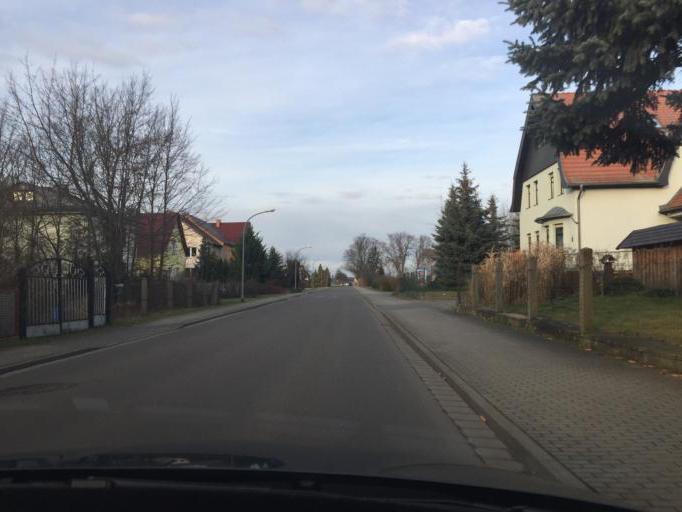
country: DE
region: Brandenburg
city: Forst
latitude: 51.7609
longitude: 14.6478
